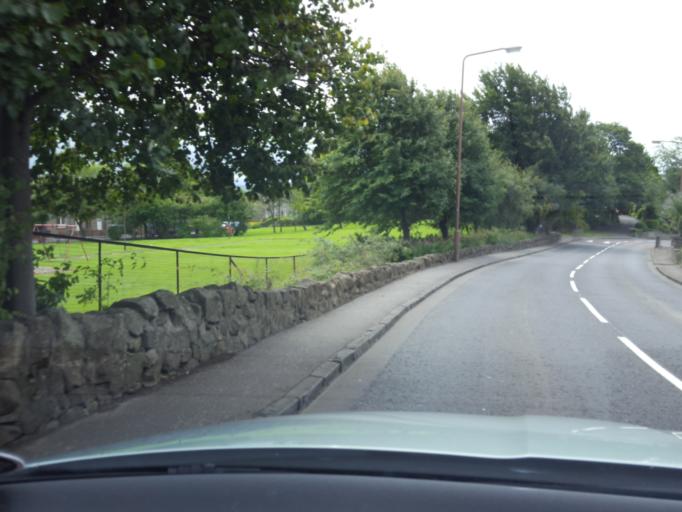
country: GB
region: Scotland
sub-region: West Lothian
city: Livingston
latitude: 55.9332
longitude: -3.5073
